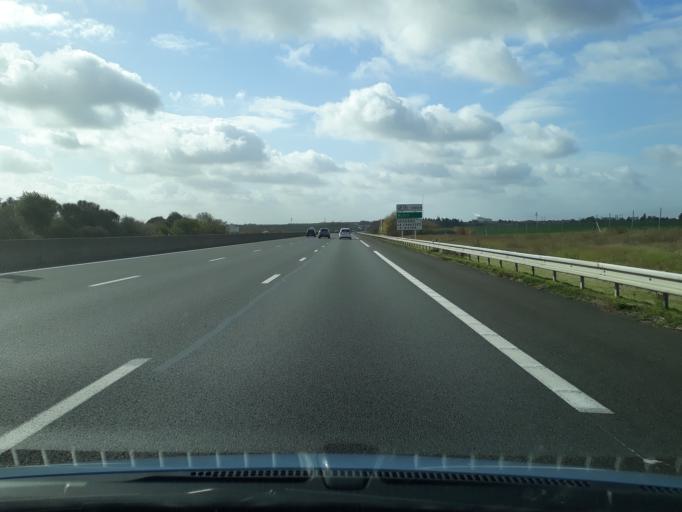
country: FR
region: Centre
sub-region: Departement du Loir-et-Cher
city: La Chaussee-Saint-Victor
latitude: 47.6358
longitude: 1.3574
